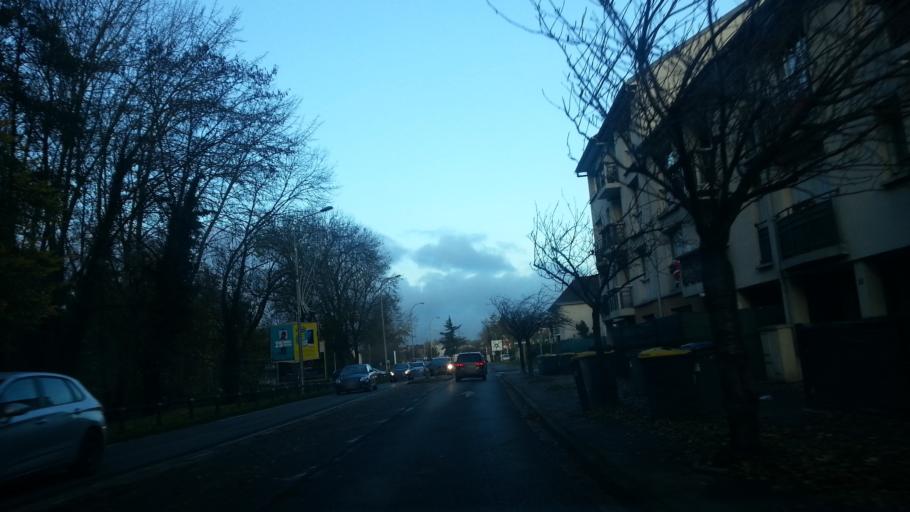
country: FR
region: Picardie
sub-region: Departement de l'Oise
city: Thiverny
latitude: 49.2543
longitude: 2.4409
